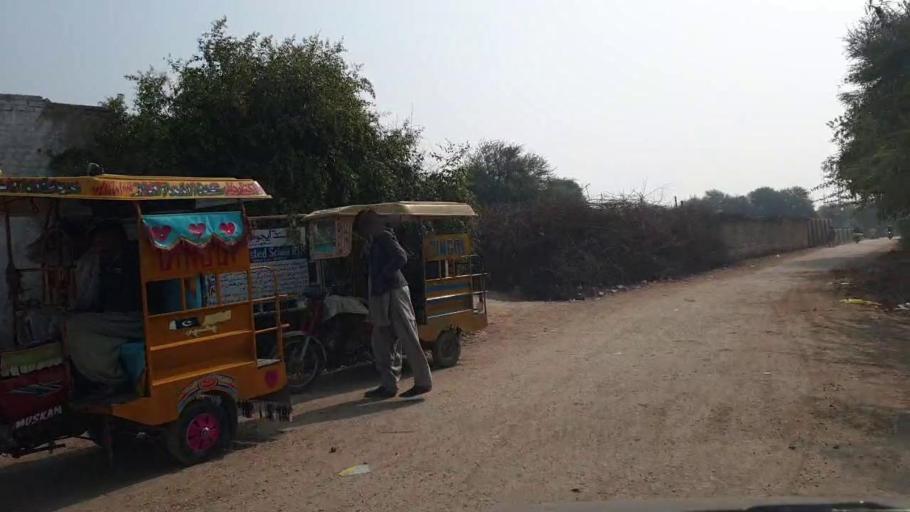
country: PK
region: Sindh
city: Bhit Shah
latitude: 25.8404
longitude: 68.4640
